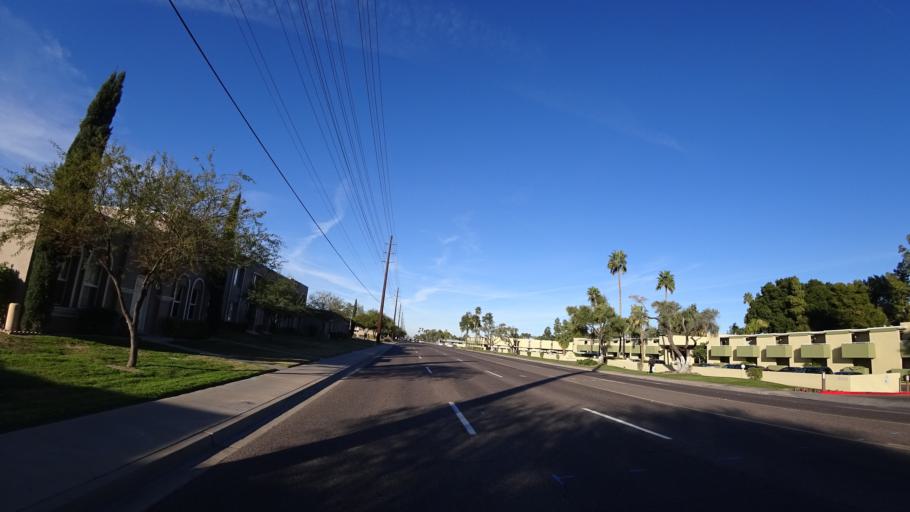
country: US
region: Arizona
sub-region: Maricopa County
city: Paradise Valley
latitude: 33.4800
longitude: -111.9531
